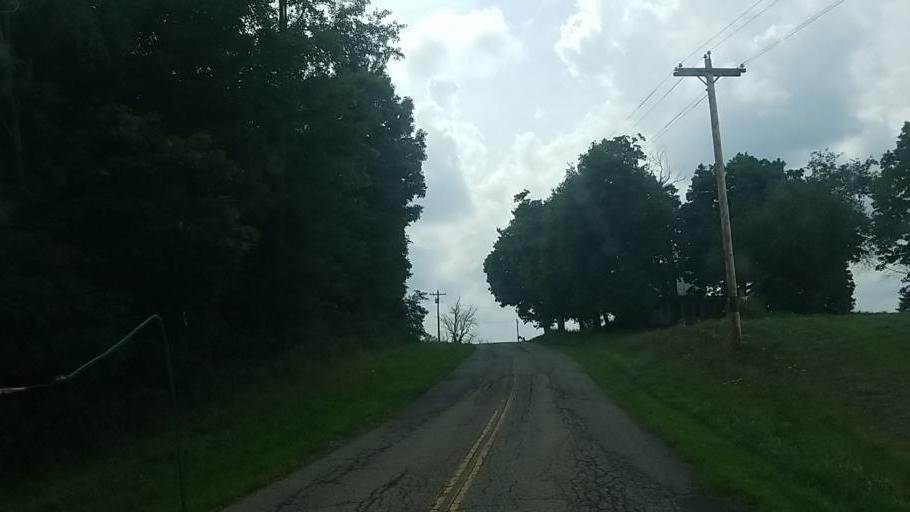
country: US
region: Ohio
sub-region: Knox County
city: Mount Vernon
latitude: 40.3161
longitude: -82.4776
